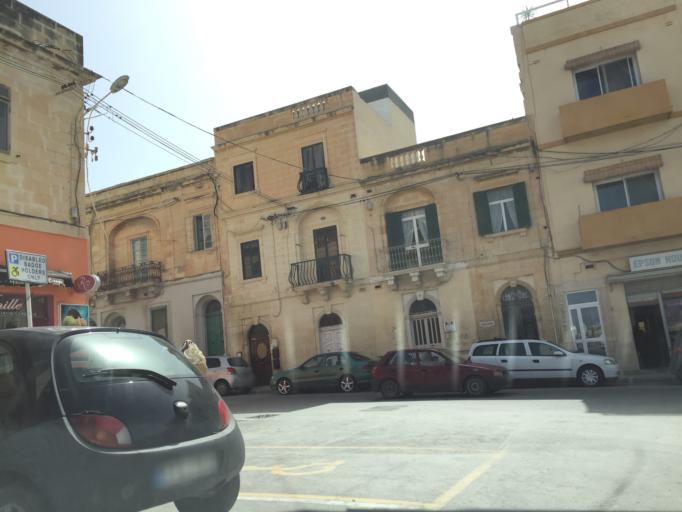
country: MT
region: Birzebbuga
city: Birzebbuga
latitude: 35.8235
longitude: 14.5286
